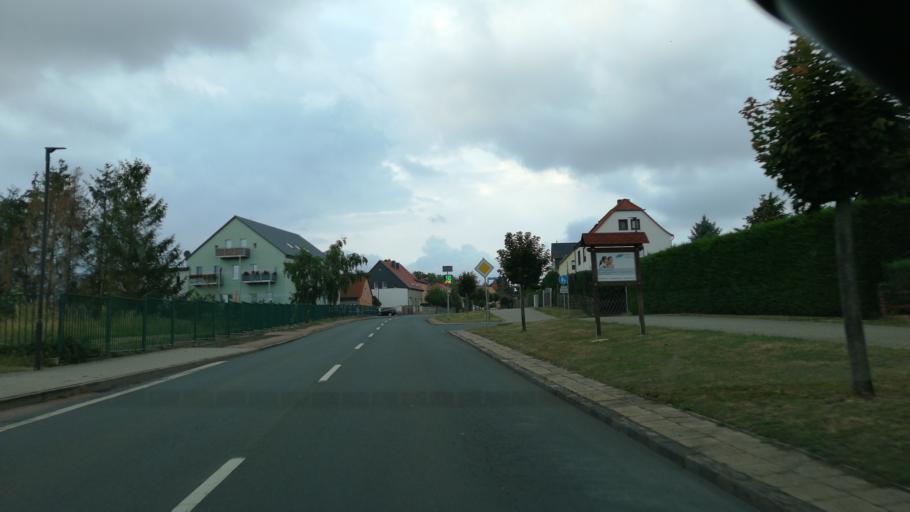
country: DE
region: Saxony-Anhalt
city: Benndorf
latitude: 51.5721
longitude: 11.4932
